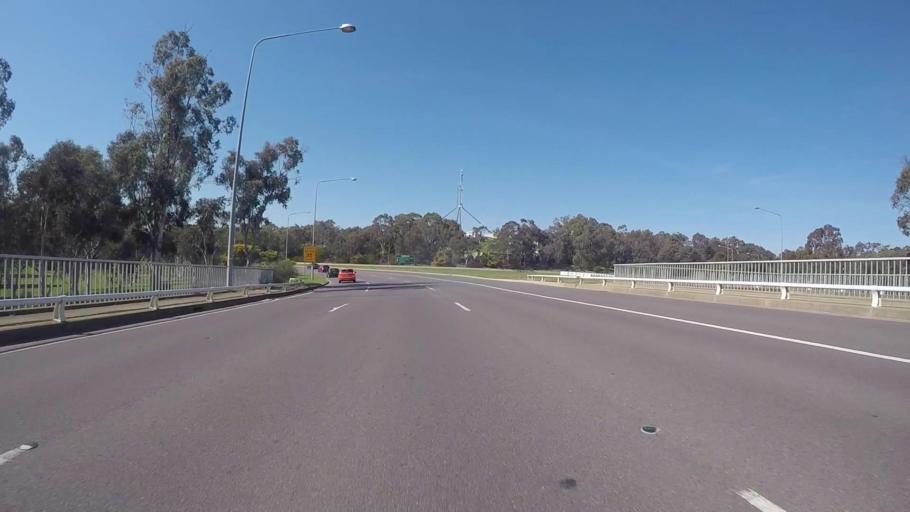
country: AU
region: Australian Capital Territory
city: Forrest
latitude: -35.3090
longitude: 149.1195
